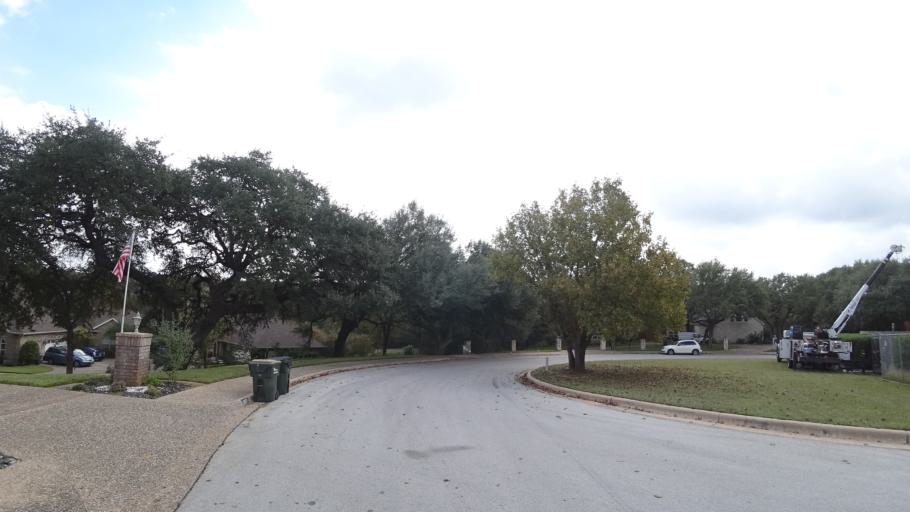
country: US
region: Texas
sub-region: Travis County
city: Barton Creek
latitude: 30.2916
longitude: -97.8990
